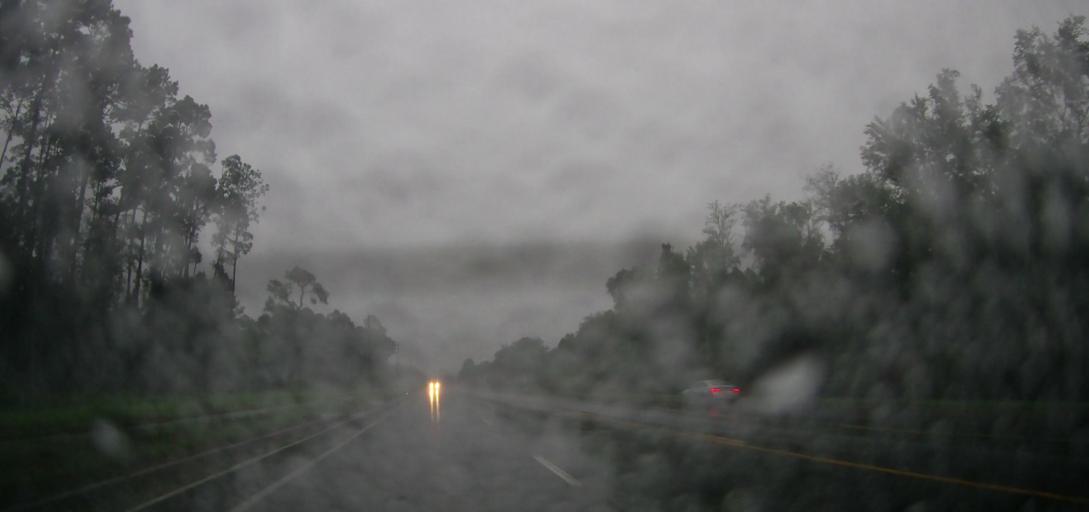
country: US
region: Georgia
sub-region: Clinch County
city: Homerville
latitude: 31.0440
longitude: -82.7270
